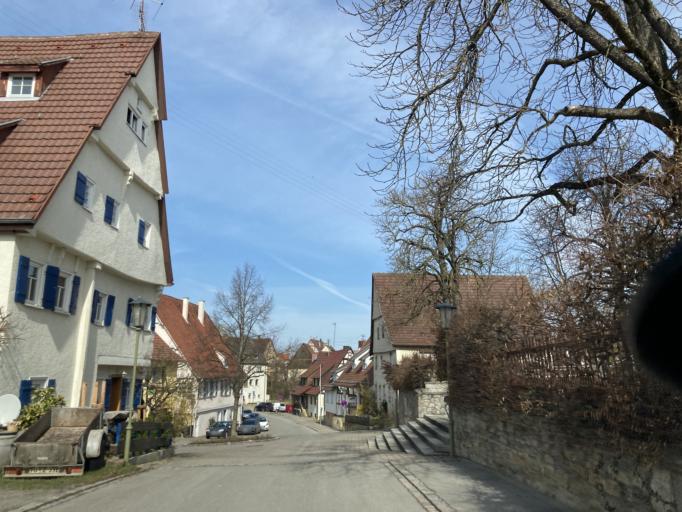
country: DE
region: Baden-Wuerttemberg
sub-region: Tuebingen Region
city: Mossingen
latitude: 48.4069
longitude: 9.0636
